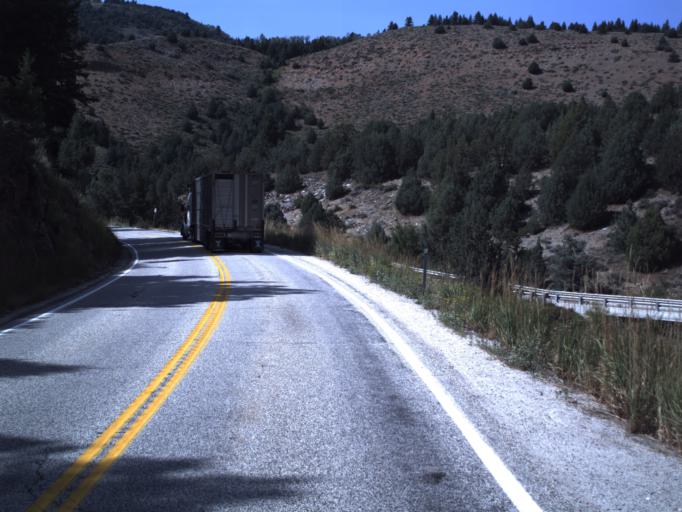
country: US
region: Utah
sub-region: Cache County
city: North Logan
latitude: 41.8348
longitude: -111.5930
